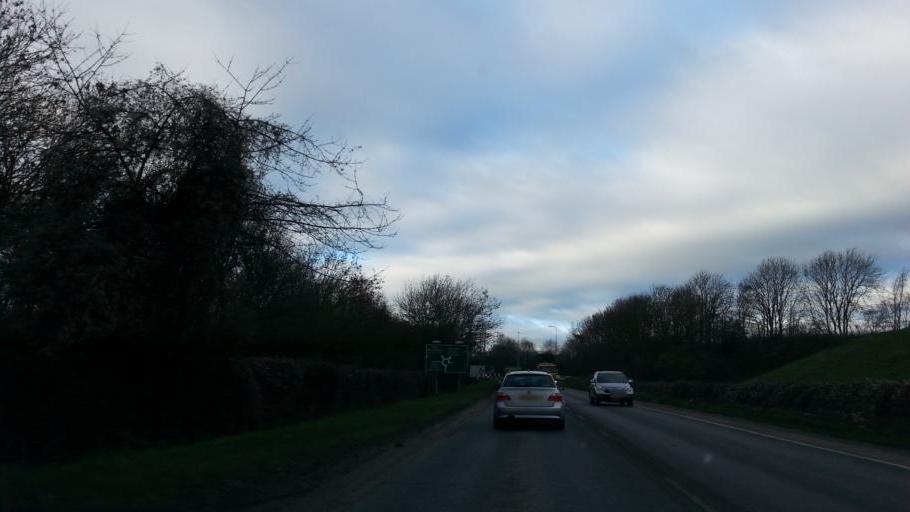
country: GB
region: England
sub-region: Suffolk
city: Bury St Edmunds
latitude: 52.2606
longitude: 0.7276
